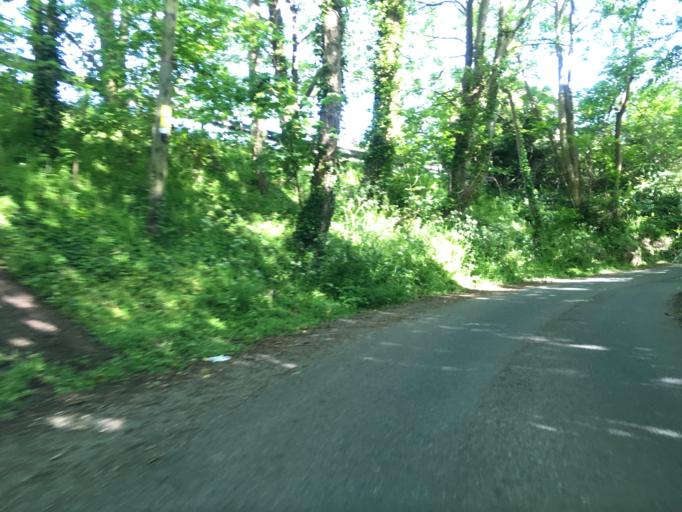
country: GB
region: England
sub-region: North Somerset
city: Portishead
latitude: 51.4782
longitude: -2.7774
